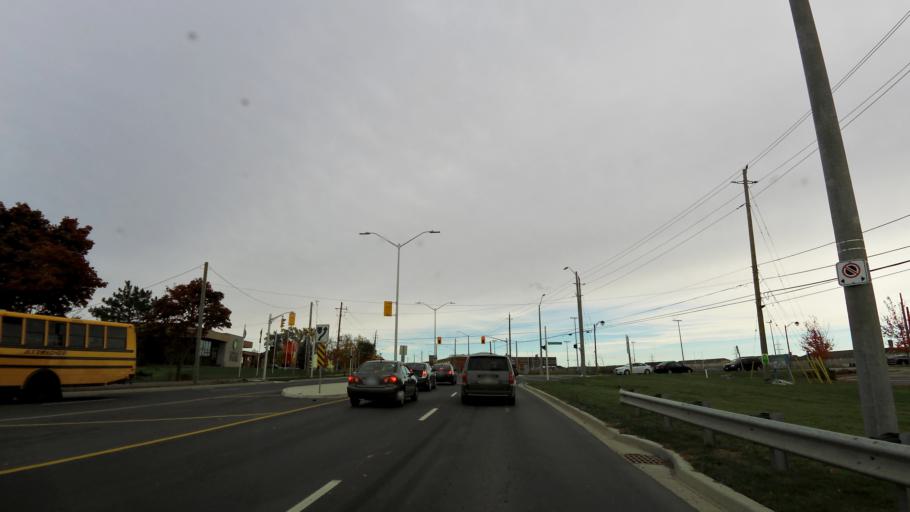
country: CA
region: Ontario
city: Hamilton
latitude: 43.1834
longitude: -79.8202
